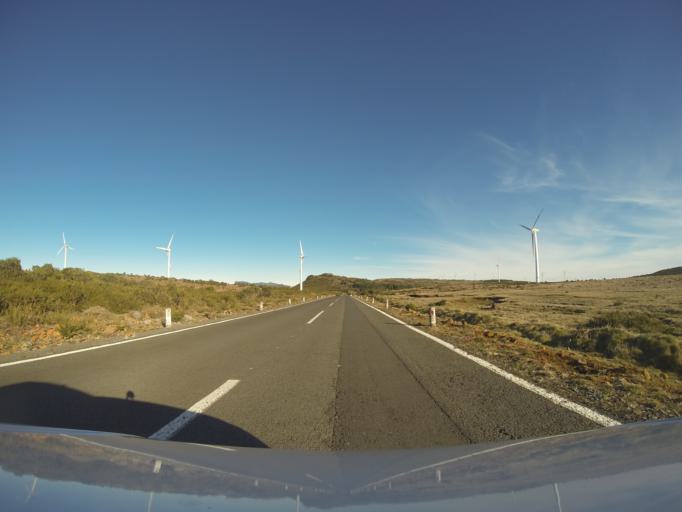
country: PT
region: Madeira
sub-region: Sao Vicente
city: Sao Vicente
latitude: 32.7599
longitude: -17.0640
